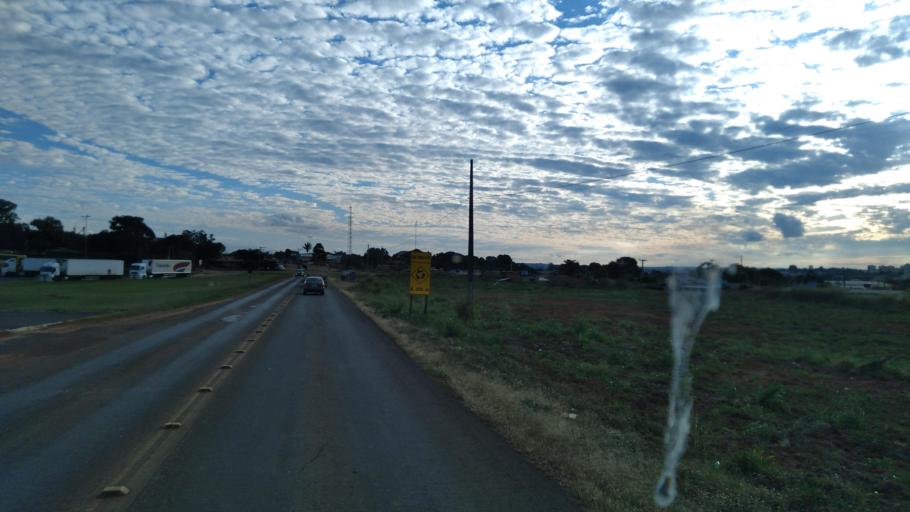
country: BR
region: Goias
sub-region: Mineiros
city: Mineiros
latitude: -17.5792
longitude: -52.5390
